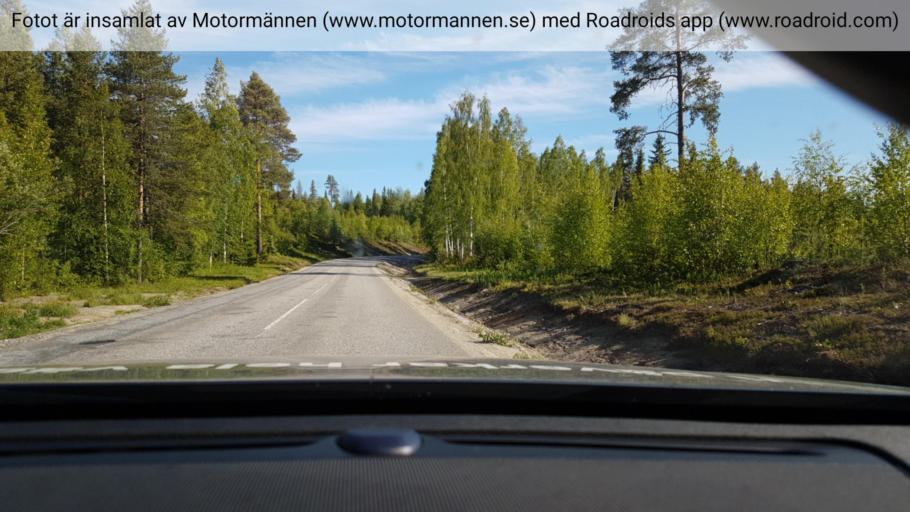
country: SE
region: Vaesterbotten
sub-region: Norsjo Kommun
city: Norsjoe
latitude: 64.6440
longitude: 19.2857
